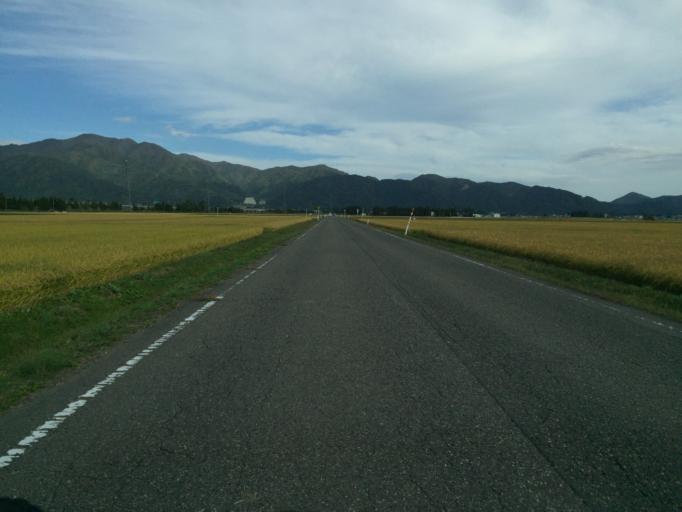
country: JP
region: Fukushima
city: Inawashiro
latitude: 37.5438
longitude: 140.0930
